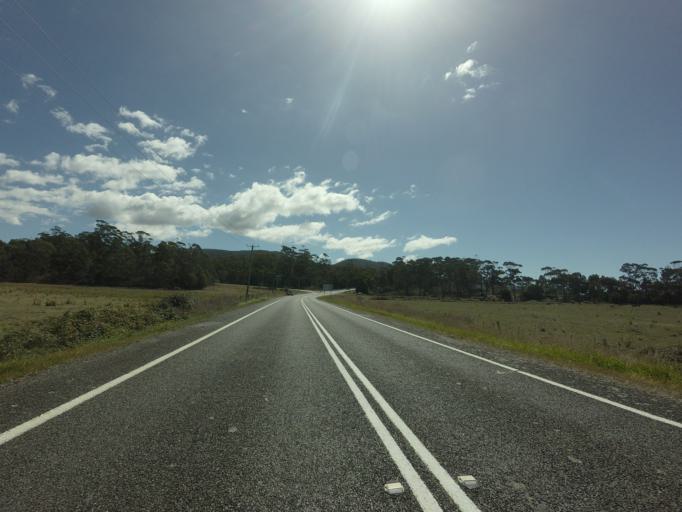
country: AU
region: Tasmania
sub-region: Break O'Day
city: St Helens
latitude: -41.6660
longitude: 148.2843
